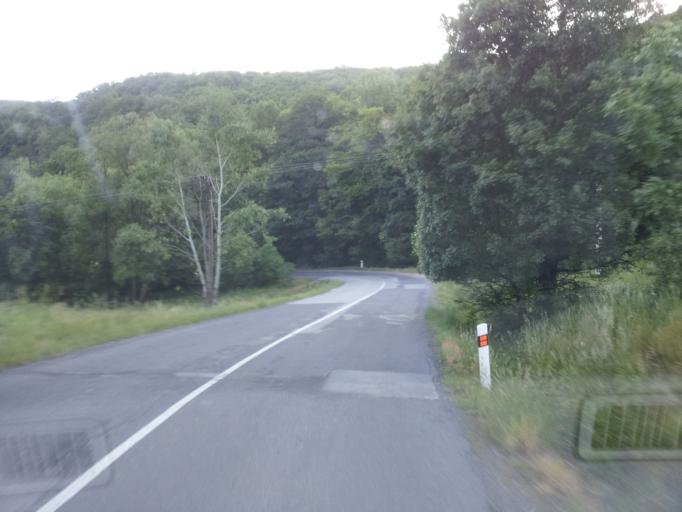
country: SK
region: Banskobystricky
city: Svaety Anton
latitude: 48.3953
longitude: 18.9352
